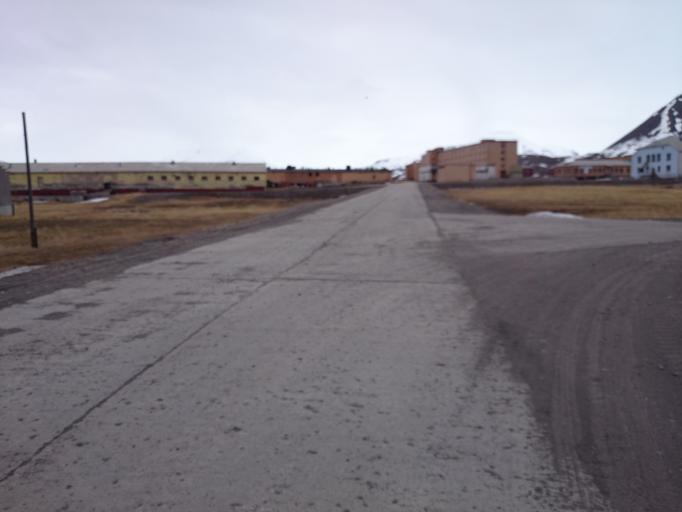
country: SJ
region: Svalbard
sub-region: Spitsbergen
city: Longyearbyen
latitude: 78.6537
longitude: 16.3306
